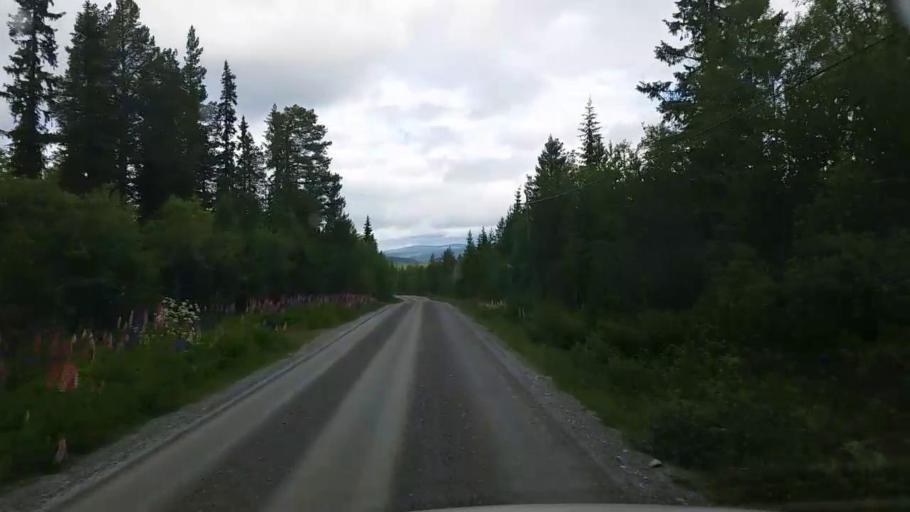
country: NO
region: Hedmark
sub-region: Engerdal
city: Engerdal
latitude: 62.4125
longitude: 12.6748
